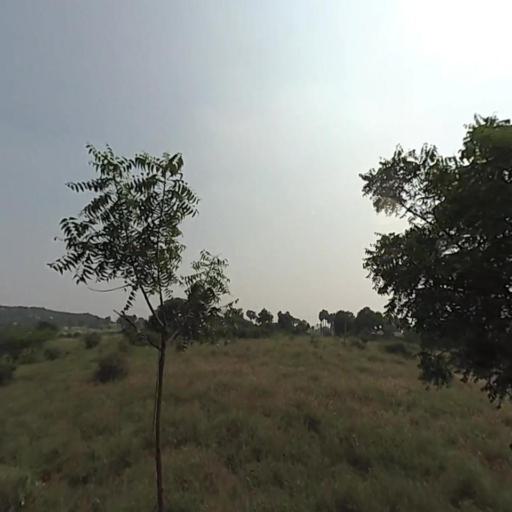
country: IN
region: Telangana
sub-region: Nalgonda
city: Nalgonda
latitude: 17.2043
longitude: 79.1518
